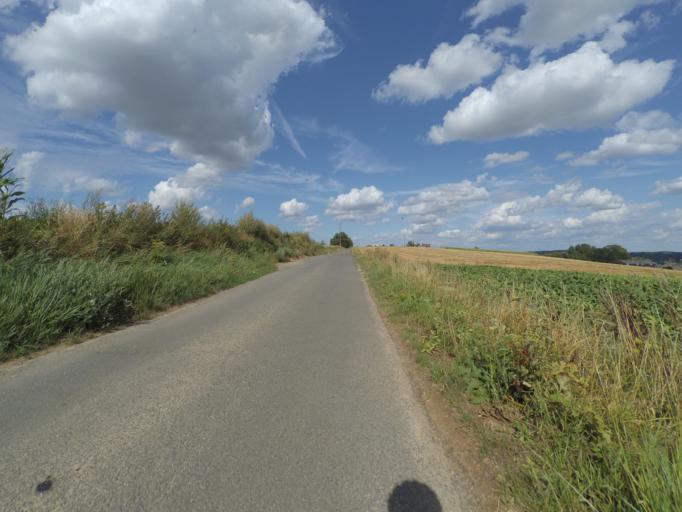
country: BE
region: Wallonia
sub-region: Province du Hainaut
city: Frasnes-lez-Buissenal
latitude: 50.6870
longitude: 3.6046
